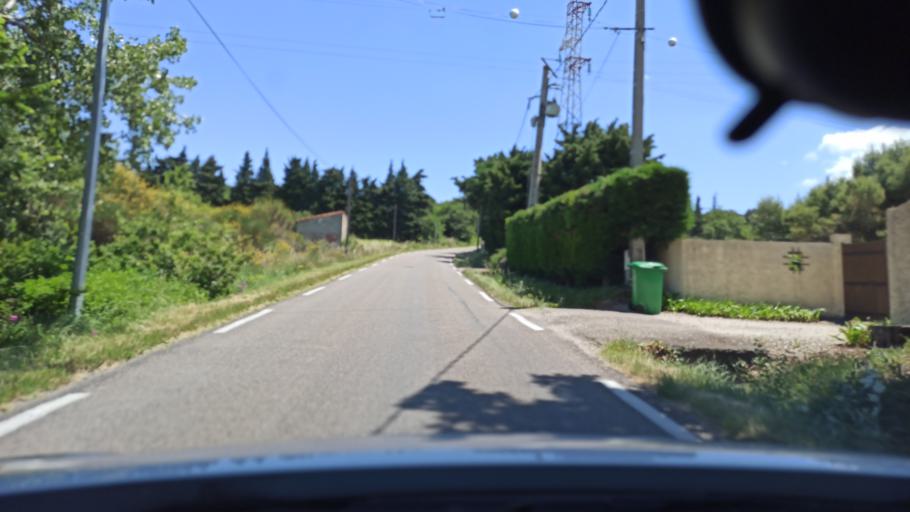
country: FR
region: Provence-Alpes-Cote d'Azur
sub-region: Departement du Vaucluse
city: Caumont-sur-Durance
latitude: 43.9070
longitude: 4.9233
